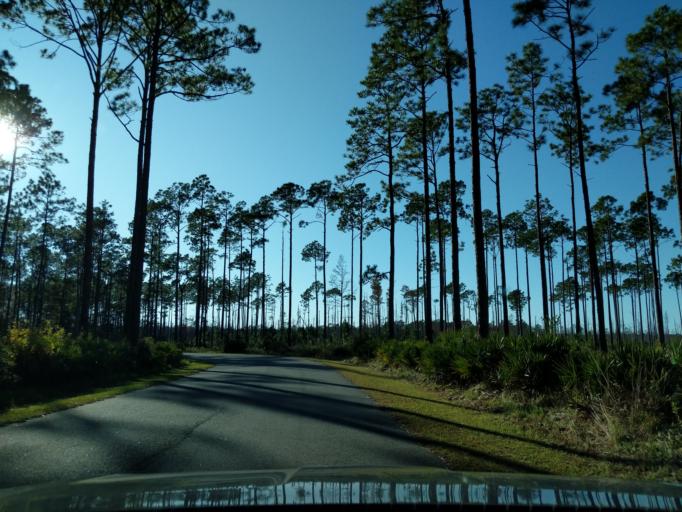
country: US
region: Georgia
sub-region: Charlton County
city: Folkston
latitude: 30.7117
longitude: -82.1430
